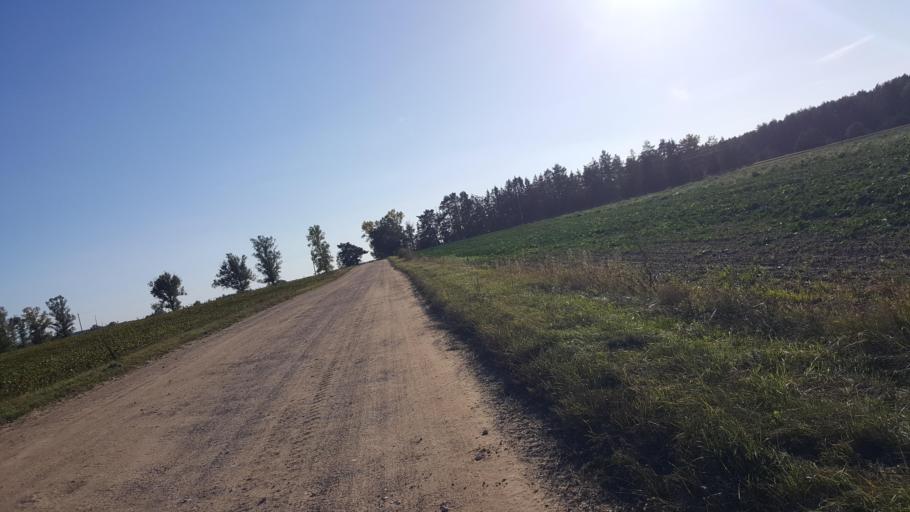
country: BY
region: Brest
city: Kamyanyets
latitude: 52.3770
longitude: 23.8790
